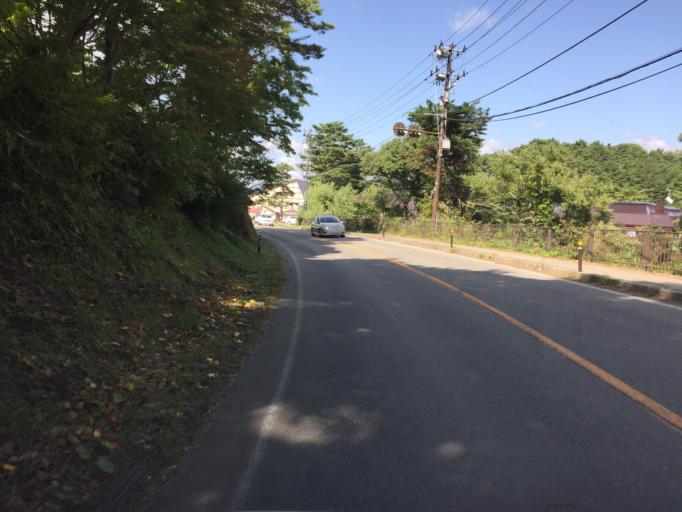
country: JP
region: Fukushima
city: Inawashiro
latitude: 37.6503
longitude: 140.0645
